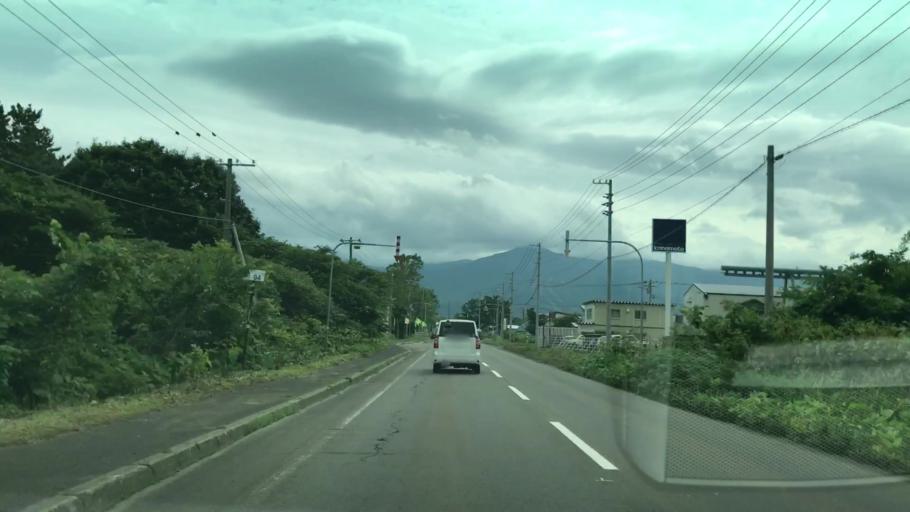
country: JP
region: Hokkaido
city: Iwanai
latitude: 43.0093
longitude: 140.5431
